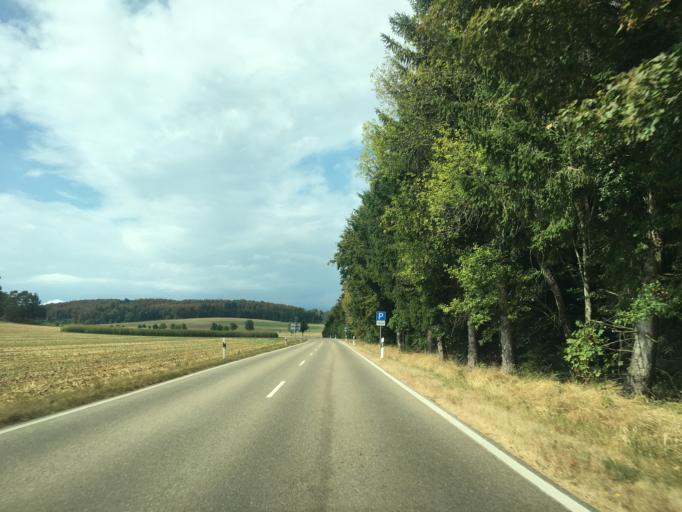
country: DE
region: Baden-Wuerttemberg
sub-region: Tuebingen Region
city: Trochtelfingen
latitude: 48.3648
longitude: 9.2525
